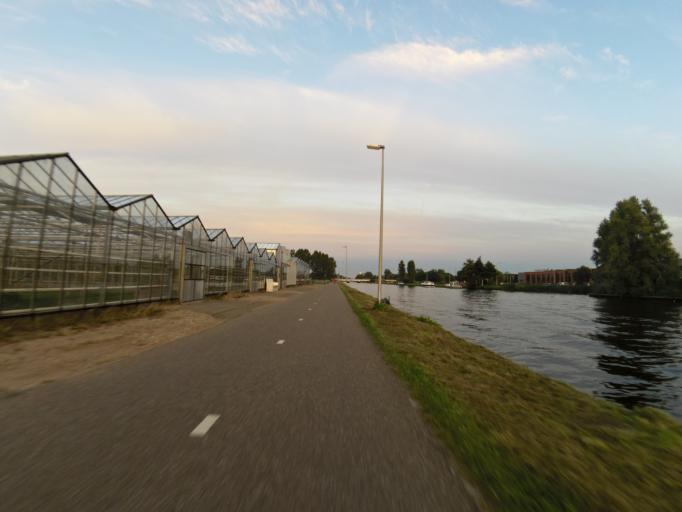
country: NL
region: South Holland
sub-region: Gemeente Katwijk
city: Rijnsburg
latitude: 52.1945
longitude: 4.4585
